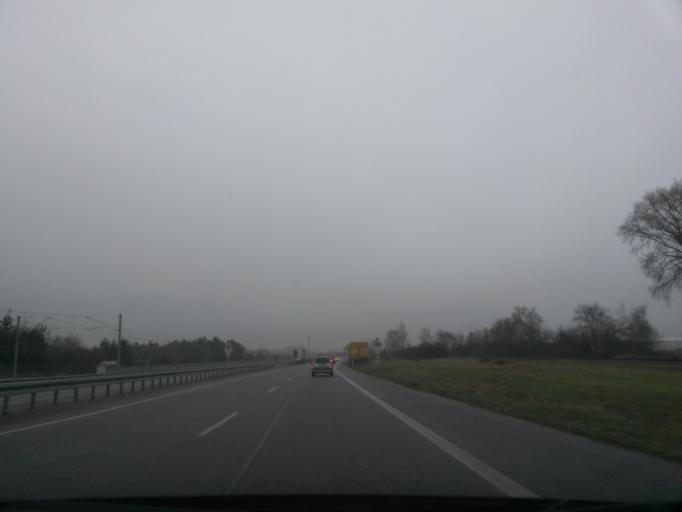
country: DE
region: Baden-Wuerttemberg
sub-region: Karlsruhe Region
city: Eggenstein-Leopoldshafen
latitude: 49.0553
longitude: 8.3916
